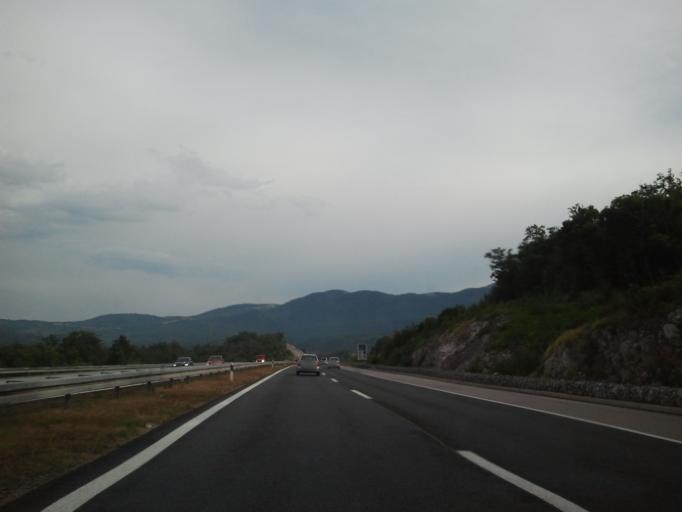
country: HR
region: Zadarska
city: Obrovac
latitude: 44.3226
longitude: 15.6750
